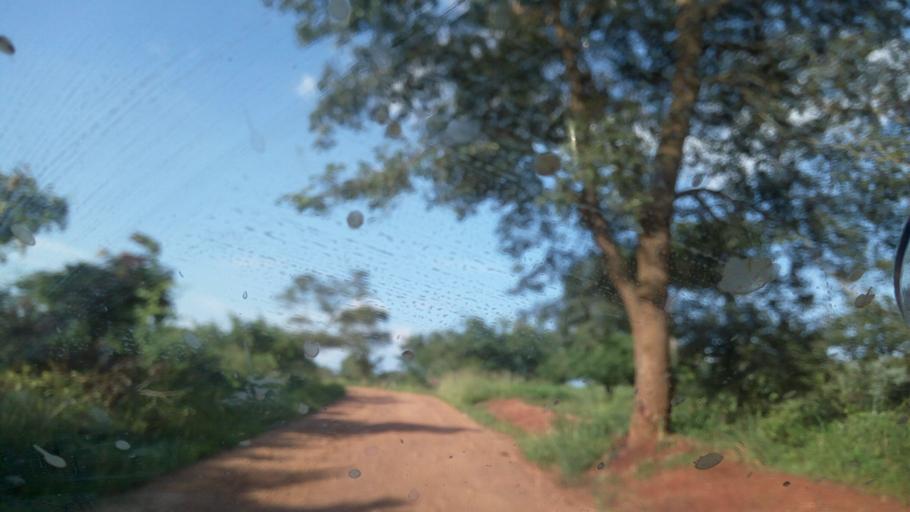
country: BI
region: Bururi
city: Rumonge
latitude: -4.2282
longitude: 28.9924
